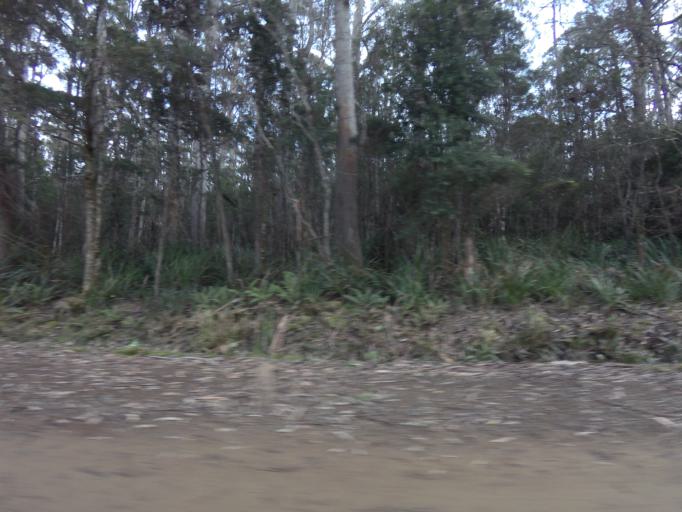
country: AU
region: Tasmania
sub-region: Huon Valley
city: Geeveston
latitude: -43.5445
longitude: 146.8896
